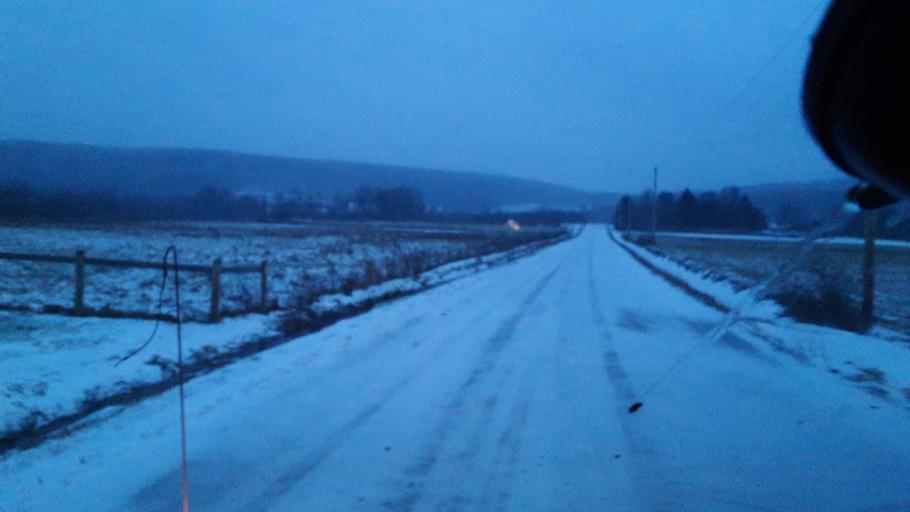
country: US
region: New York
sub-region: Allegany County
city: Friendship
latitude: 42.3005
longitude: -78.1625
